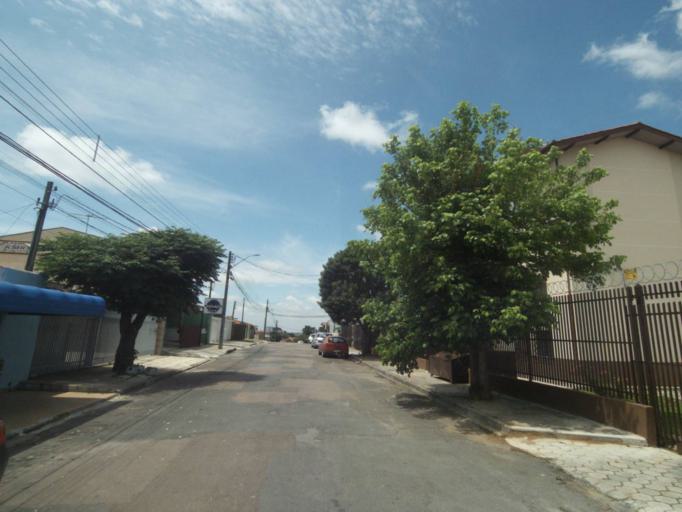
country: BR
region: Parana
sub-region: Curitiba
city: Curitiba
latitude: -25.4530
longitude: -49.3524
